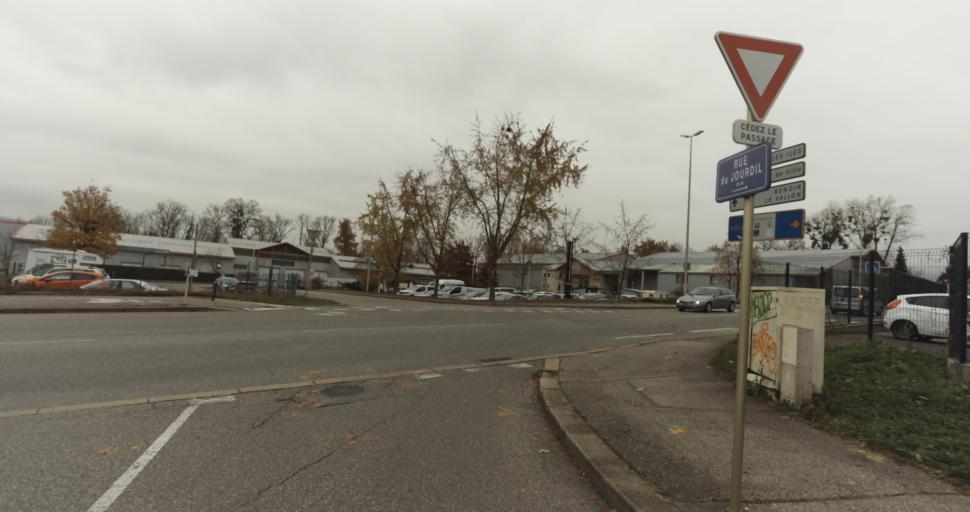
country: FR
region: Rhone-Alpes
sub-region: Departement de la Haute-Savoie
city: Cran-Gevrier
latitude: 45.9059
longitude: 6.0917
